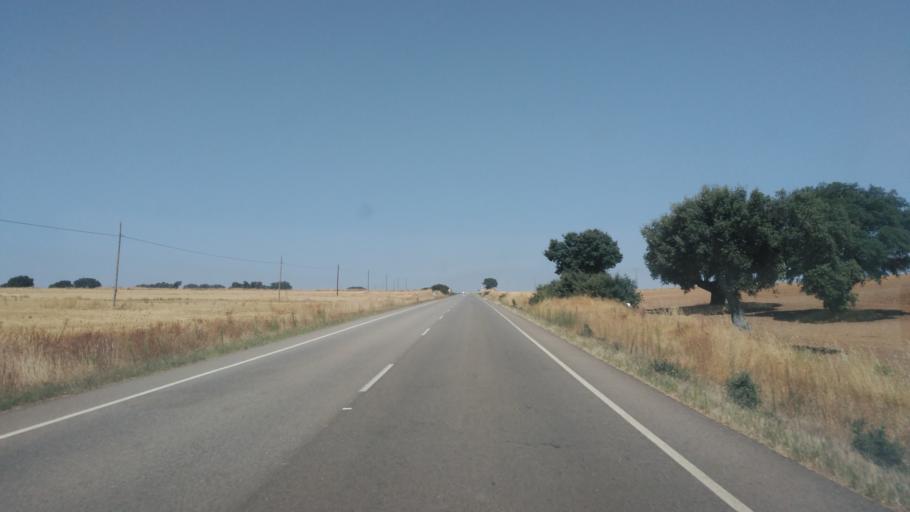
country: ES
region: Castille and Leon
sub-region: Provincia de Salamanca
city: Cabrillas
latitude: 40.7506
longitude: -6.1850
